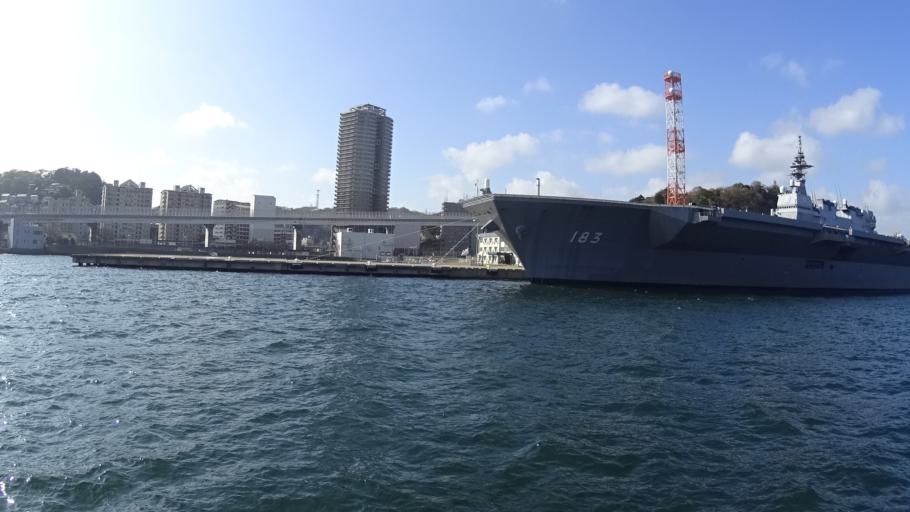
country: JP
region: Kanagawa
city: Yokosuka
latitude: 35.2869
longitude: 139.6560
